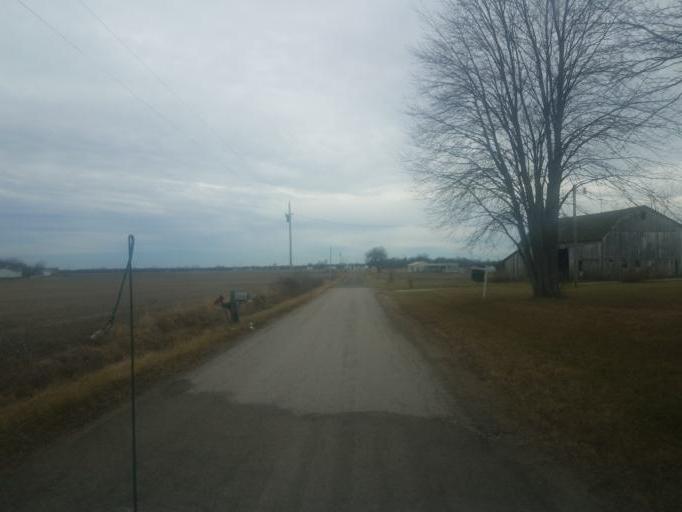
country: US
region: Ohio
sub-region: Morrow County
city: Mount Gilead
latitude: 40.6263
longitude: -82.9130
